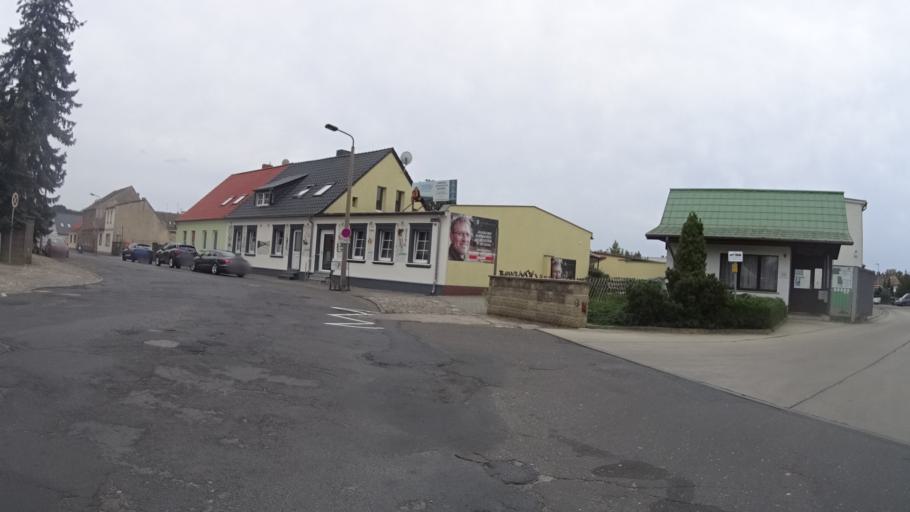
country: DE
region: Brandenburg
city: Luckenwalde
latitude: 52.0834
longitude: 13.1607
